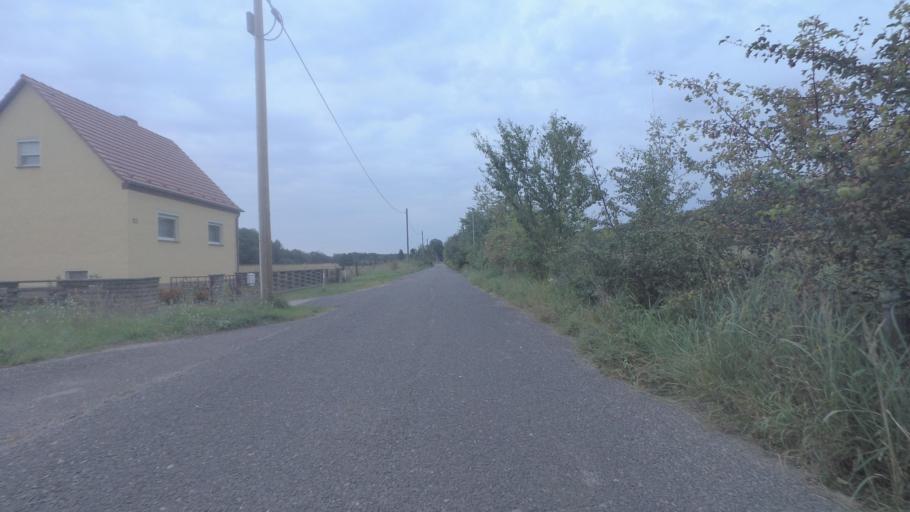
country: DE
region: Brandenburg
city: Michendorf
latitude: 52.3344
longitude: 13.0996
